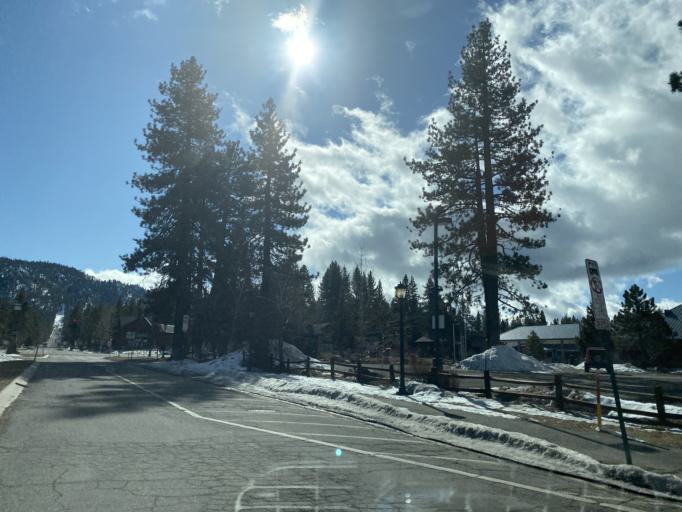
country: US
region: California
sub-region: El Dorado County
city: South Lake Tahoe
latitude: 38.9494
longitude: -119.9582
